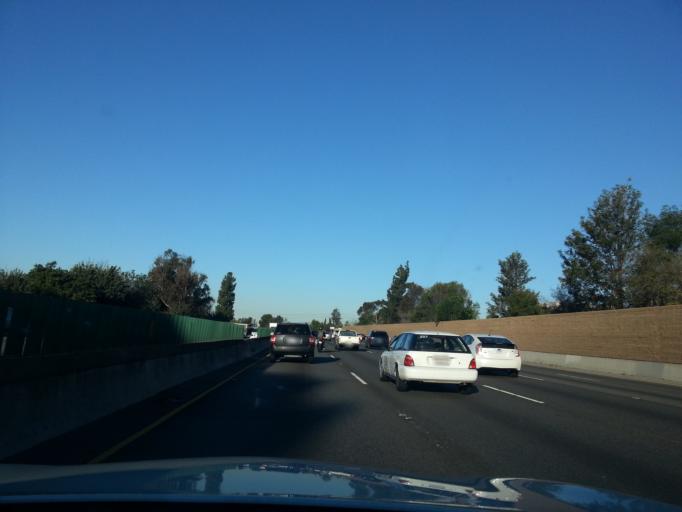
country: US
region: California
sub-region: Los Angeles County
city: Sherman Oaks
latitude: 34.1568
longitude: -118.4191
